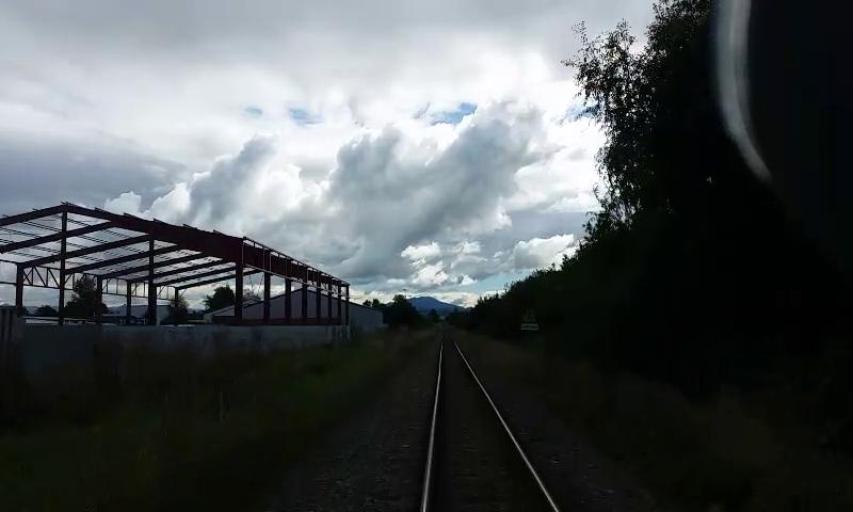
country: NZ
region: Canterbury
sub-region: Waimakariri District
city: Woodend
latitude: -43.3141
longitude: 172.6009
